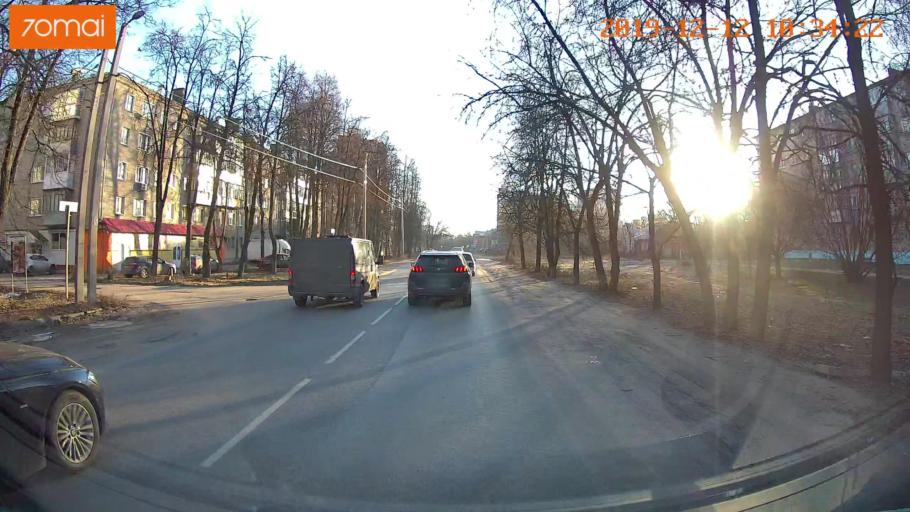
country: RU
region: Ivanovo
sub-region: Gorod Ivanovo
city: Ivanovo
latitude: 56.9900
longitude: 40.9730
